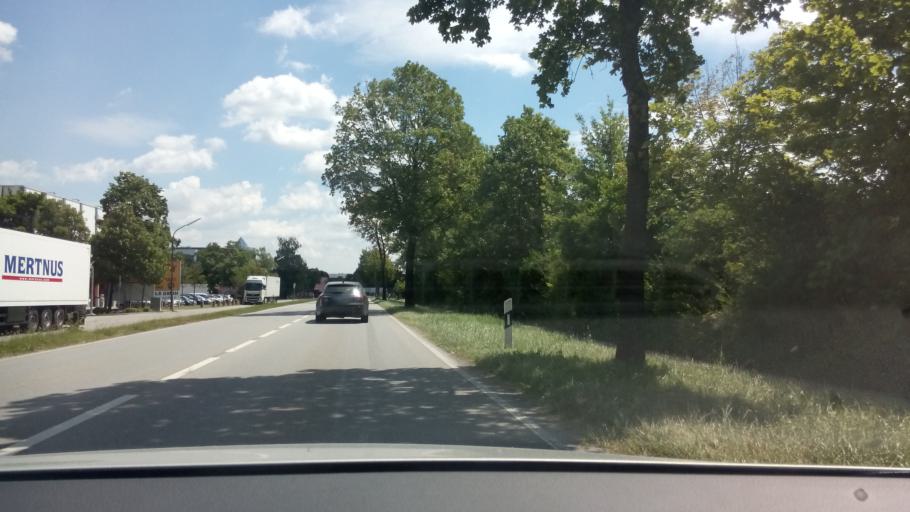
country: DE
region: Bavaria
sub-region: Upper Bavaria
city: Garching bei Munchen
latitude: 48.2503
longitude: 11.6139
